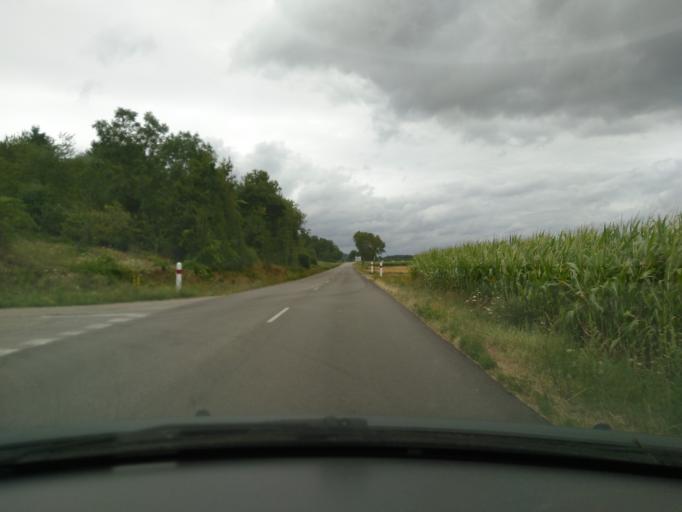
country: FR
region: Rhone-Alpes
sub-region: Departement de l'Isere
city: Champier
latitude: 45.4361
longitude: 5.2788
